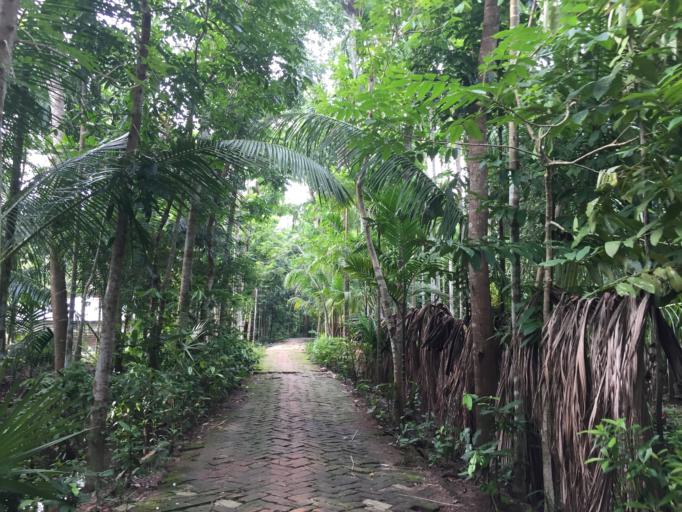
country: BD
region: Barisal
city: Mathba
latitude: 22.1914
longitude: 89.9248
